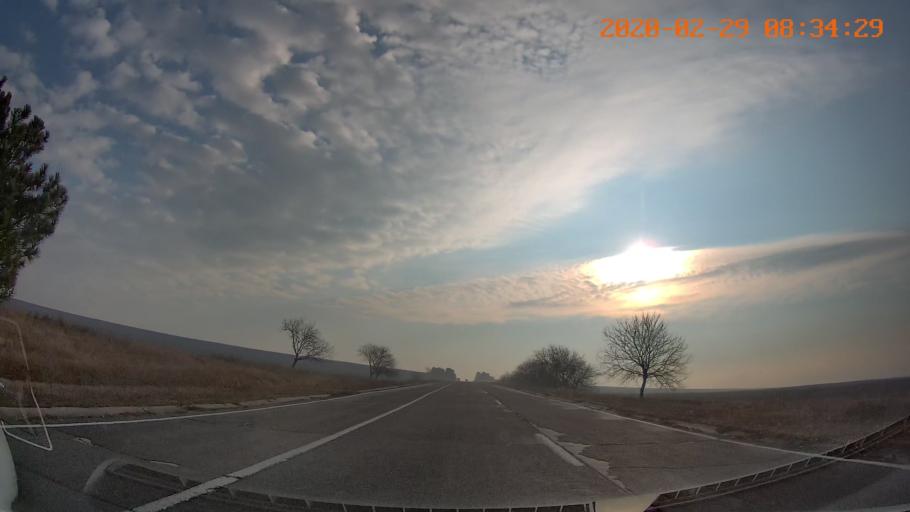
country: MD
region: Anenii Noi
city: Anenii Noi
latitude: 46.9248
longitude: 29.3099
